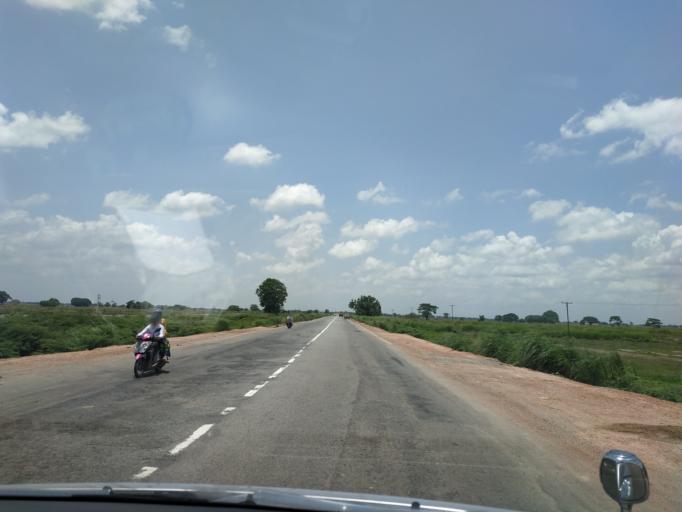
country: MM
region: Bago
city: Thanatpin
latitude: 17.4494
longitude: 96.6310
